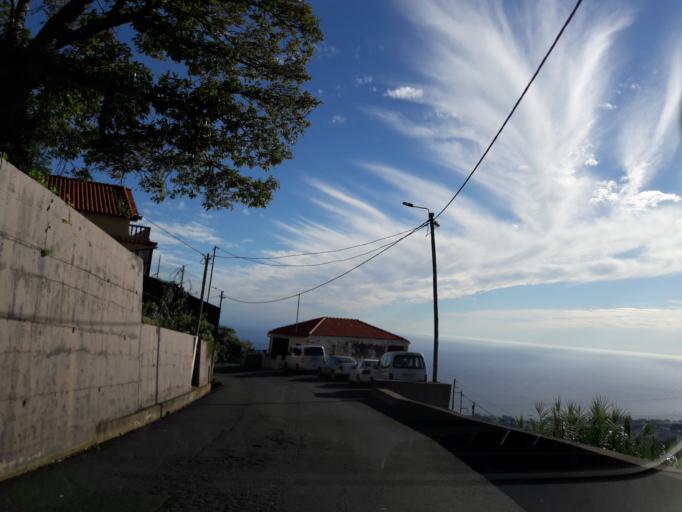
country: PT
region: Madeira
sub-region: Funchal
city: Nossa Senhora do Monte
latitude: 32.6772
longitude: -16.9116
